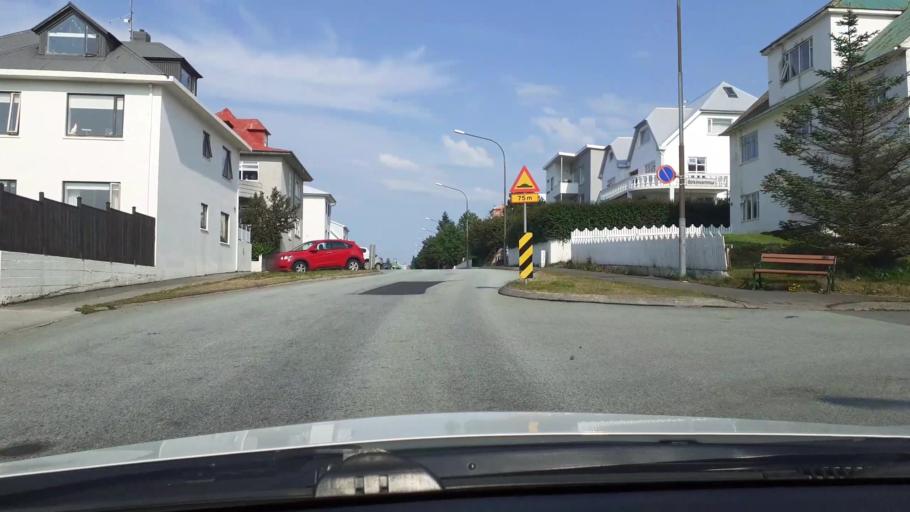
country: IS
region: Capital Region
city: Hafnarfjoerdur
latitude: 64.0615
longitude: -21.9588
